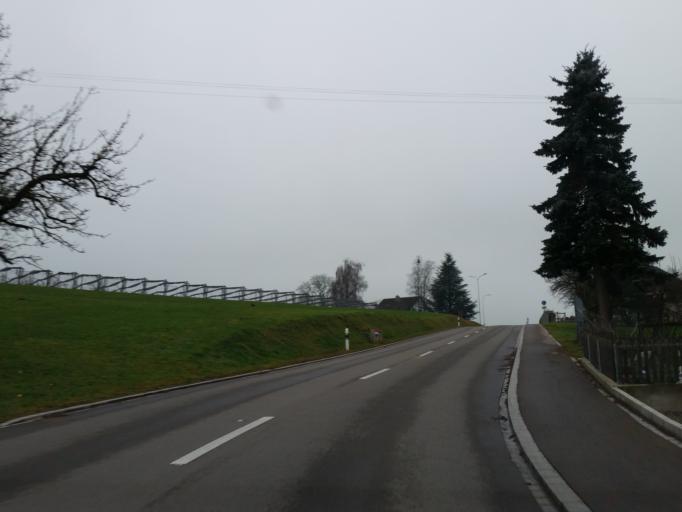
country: CH
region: Thurgau
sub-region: Weinfelden District
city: Erlen
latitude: 47.5383
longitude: 9.2326
